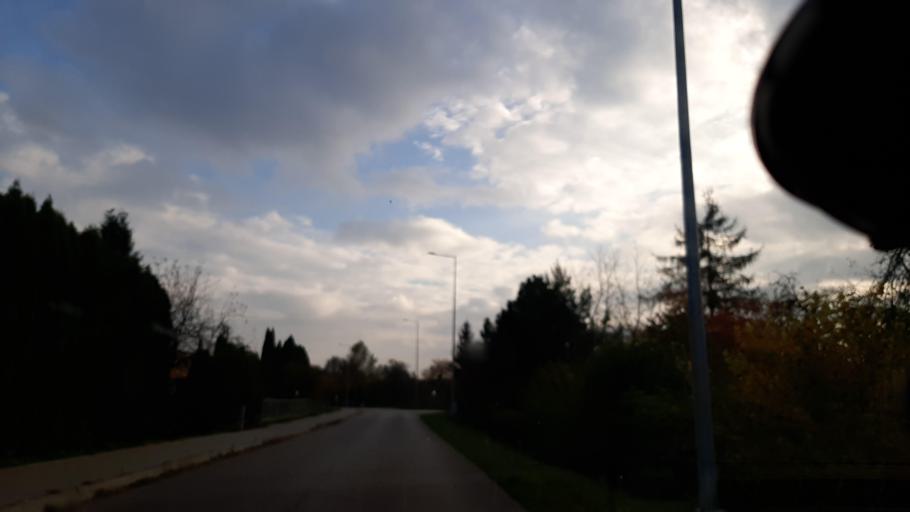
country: PL
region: Lublin Voivodeship
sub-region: Powiat pulawski
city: Naleczow
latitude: 51.3156
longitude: 22.2134
